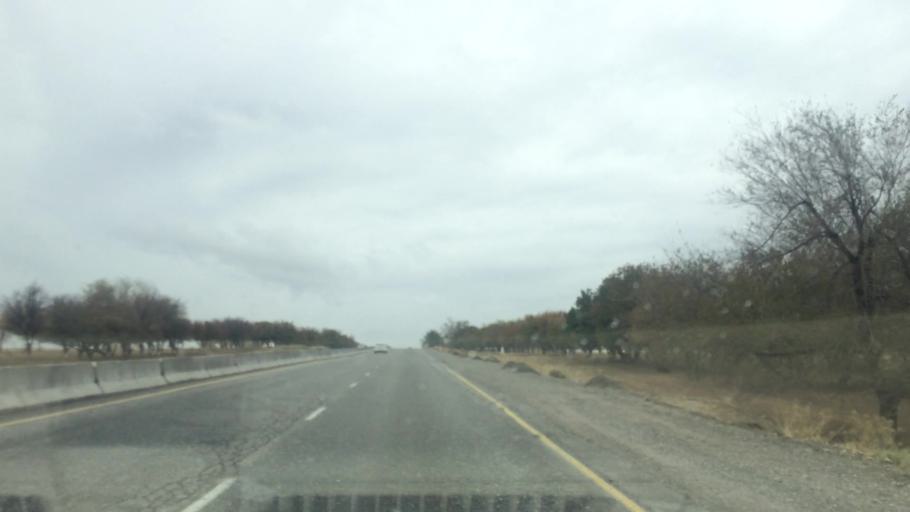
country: UZ
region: Samarqand
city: Bulung'ur
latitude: 39.8614
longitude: 67.4708
